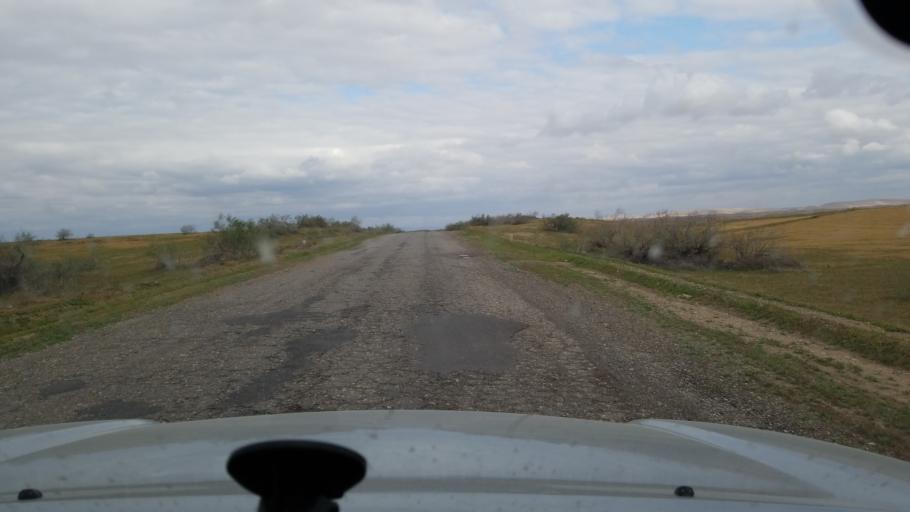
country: TM
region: Mary
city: Serhetabat
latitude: 35.9841
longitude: 62.6349
